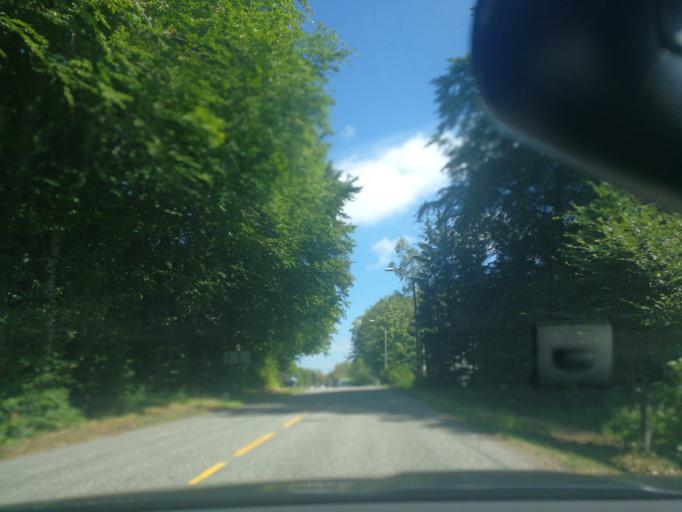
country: NO
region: Vestfold
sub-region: Sandefjord
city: Sandefjord
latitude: 59.1938
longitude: 10.2293
